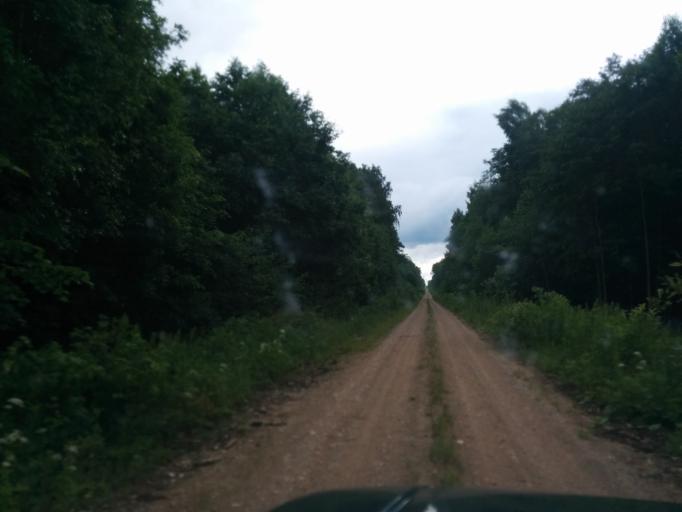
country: LV
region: Vilaka
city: Vilaka
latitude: 57.3927
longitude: 27.5948
